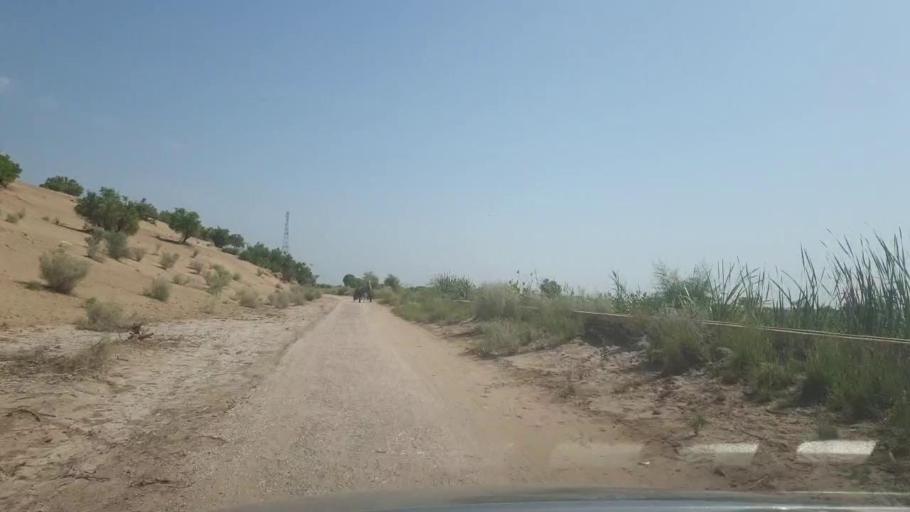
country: PK
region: Sindh
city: Khairpur
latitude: 27.3956
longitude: 69.0778
